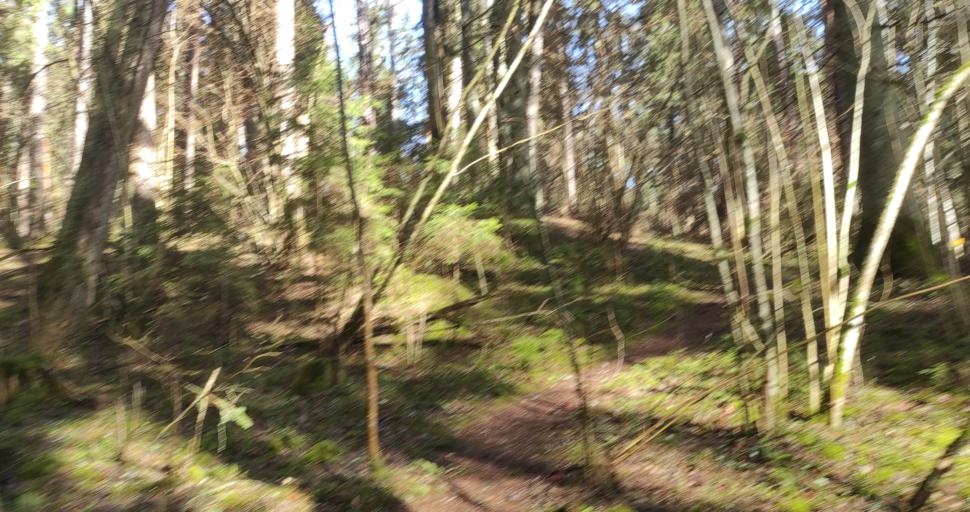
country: LV
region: Tukuma Rajons
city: Tukums
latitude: 57.1146
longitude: 23.0374
